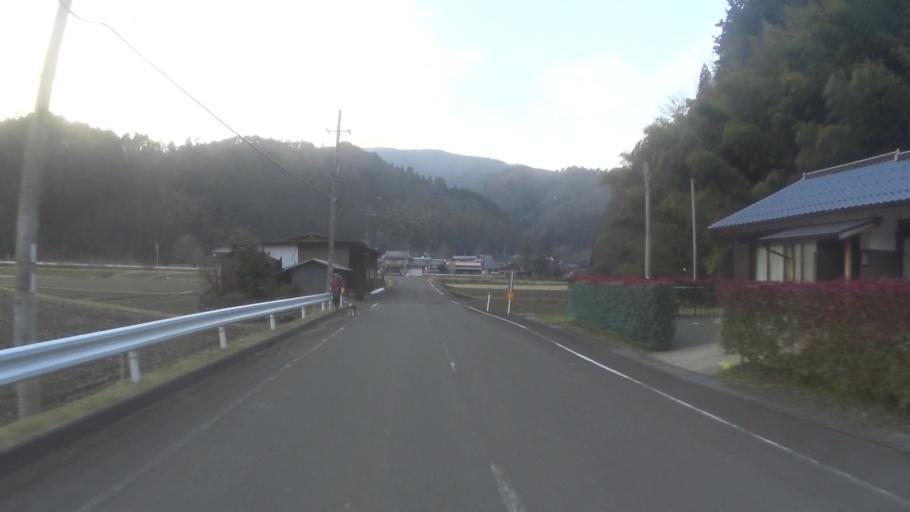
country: JP
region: Kyoto
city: Maizuru
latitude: 35.3863
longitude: 135.4627
